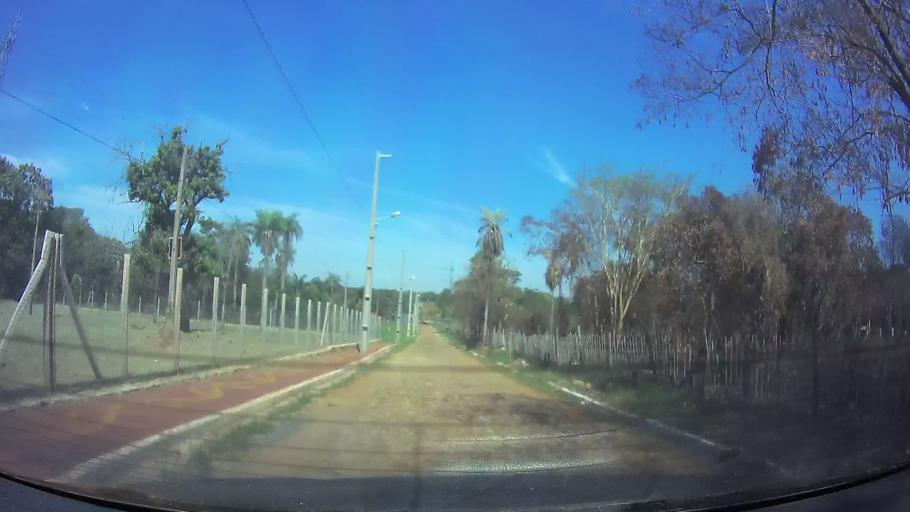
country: PY
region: Central
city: Limpio
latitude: -25.2347
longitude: -57.4382
